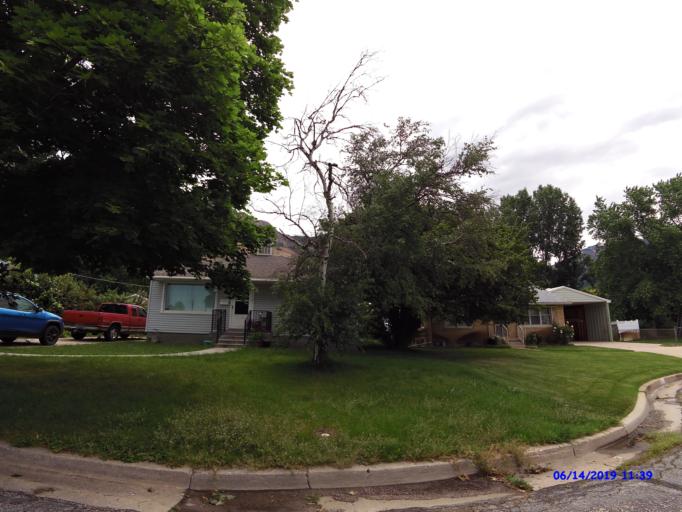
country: US
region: Utah
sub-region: Weber County
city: Ogden
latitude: 41.2498
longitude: -111.9410
